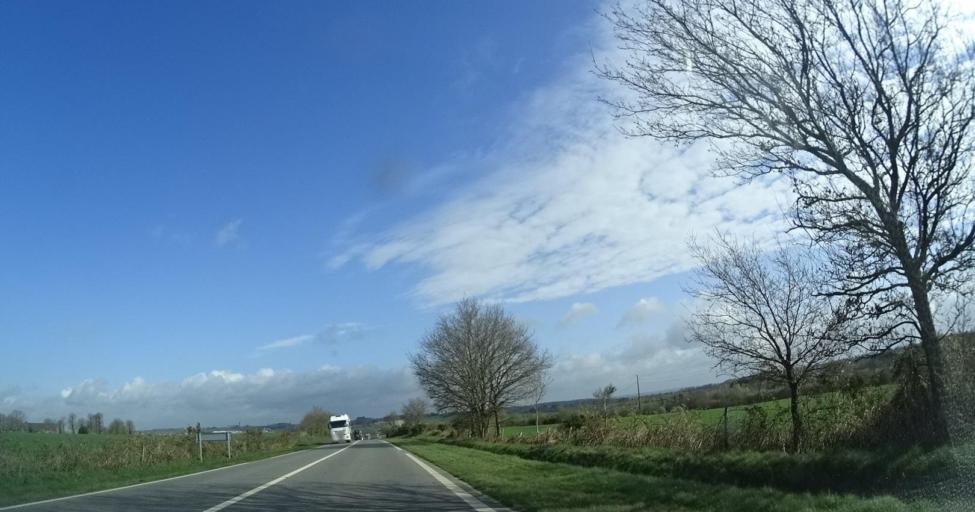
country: FR
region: Brittany
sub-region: Departement d'Ille-et-Vilaine
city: Pipriac
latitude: 47.7862
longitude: -1.9261
